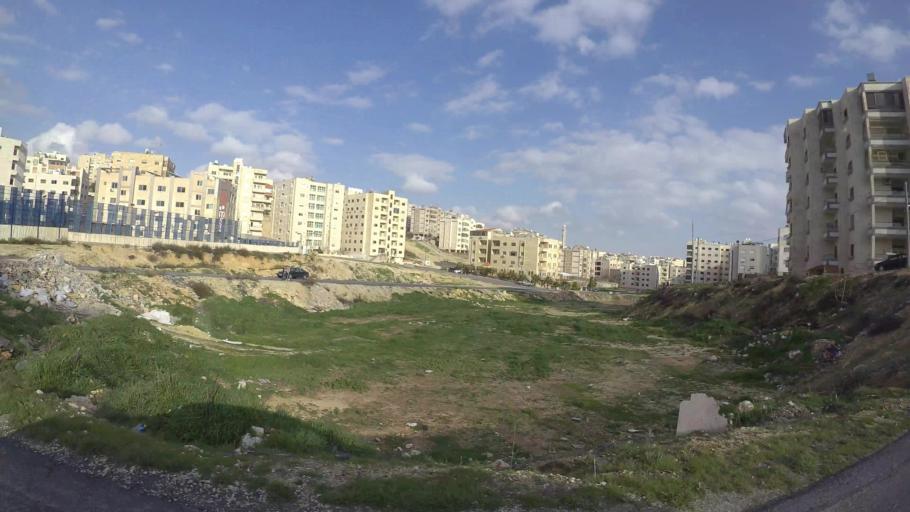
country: JO
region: Amman
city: Al Jubayhah
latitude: 32.0094
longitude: 35.8594
